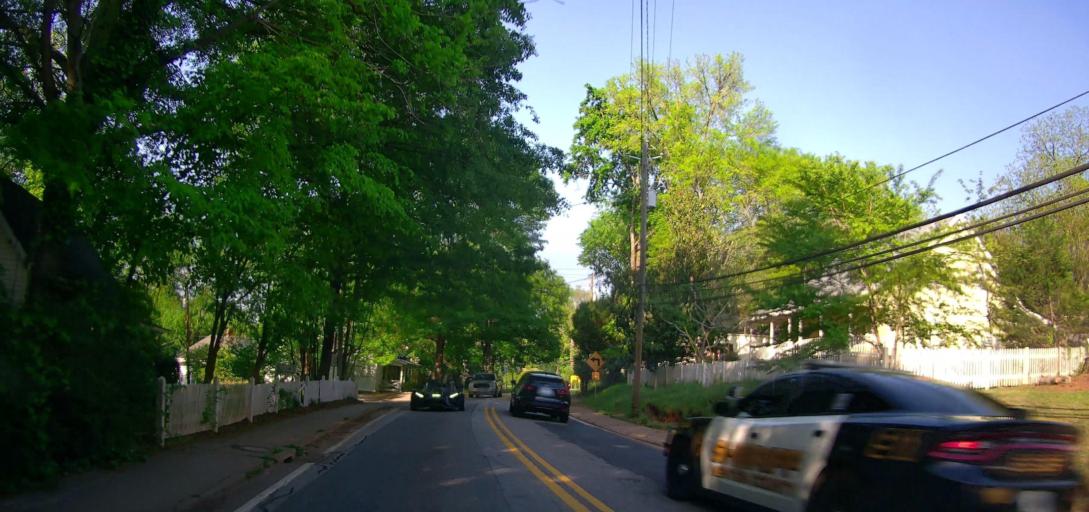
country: US
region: Georgia
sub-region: Newton County
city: Porterdale
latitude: 33.5673
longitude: -83.8992
